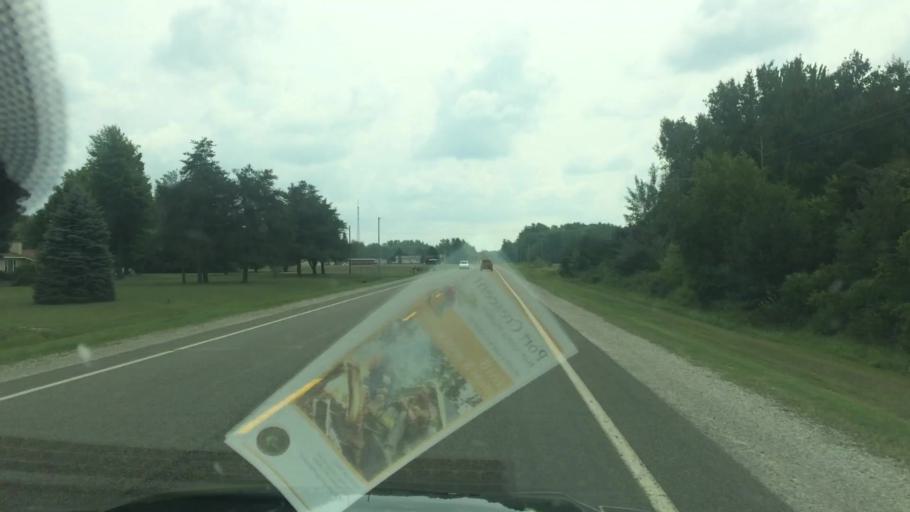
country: US
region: Michigan
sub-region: Tuscola County
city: Cass City
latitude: 43.6586
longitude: -83.0983
